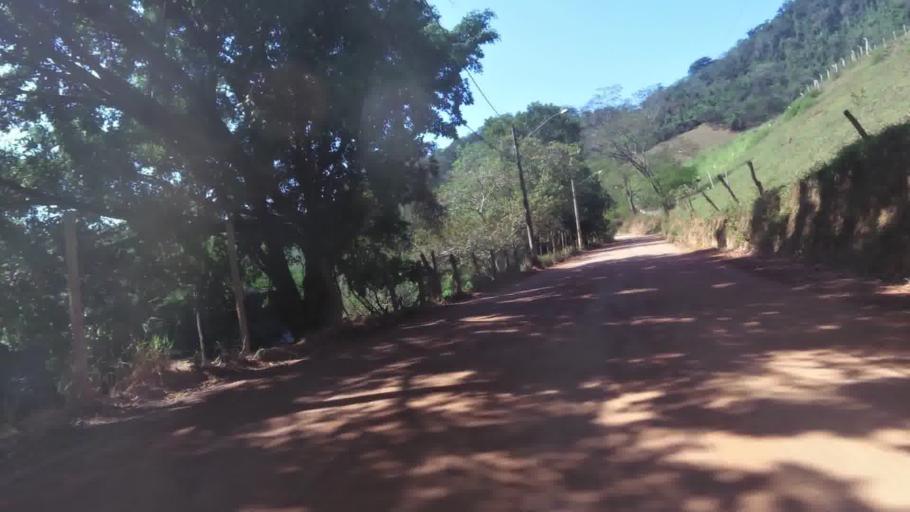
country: BR
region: Espirito Santo
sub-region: Alfredo Chaves
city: Alfredo Chaves
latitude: -20.6321
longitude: -40.7631
